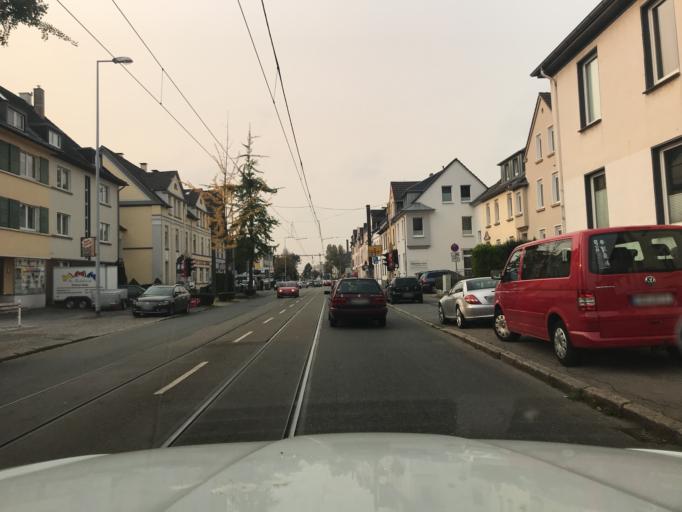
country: DE
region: North Rhine-Westphalia
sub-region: Regierungsbezirk Dusseldorf
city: Muelheim (Ruhr)
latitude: 51.4178
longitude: 6.9017
